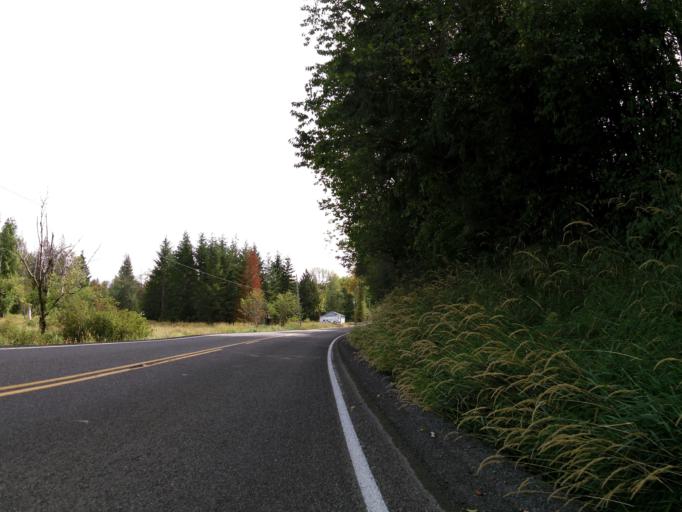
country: US
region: Washington
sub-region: Lewis County
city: Napavine
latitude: 46.5608
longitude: -122.9629
